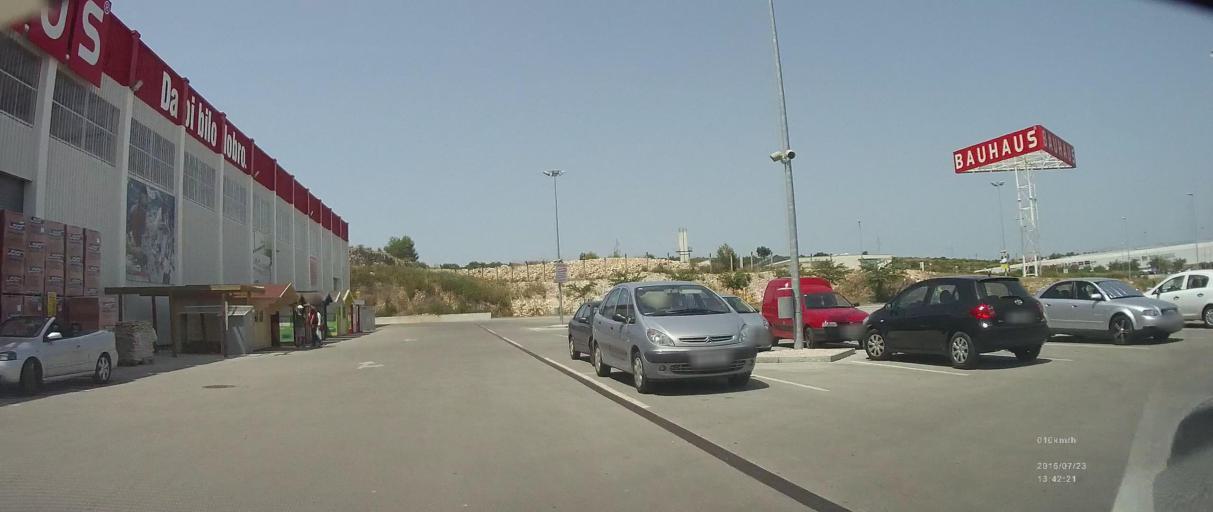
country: HR
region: Zadarska
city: Zadar
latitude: 44.1136
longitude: 15.2702
